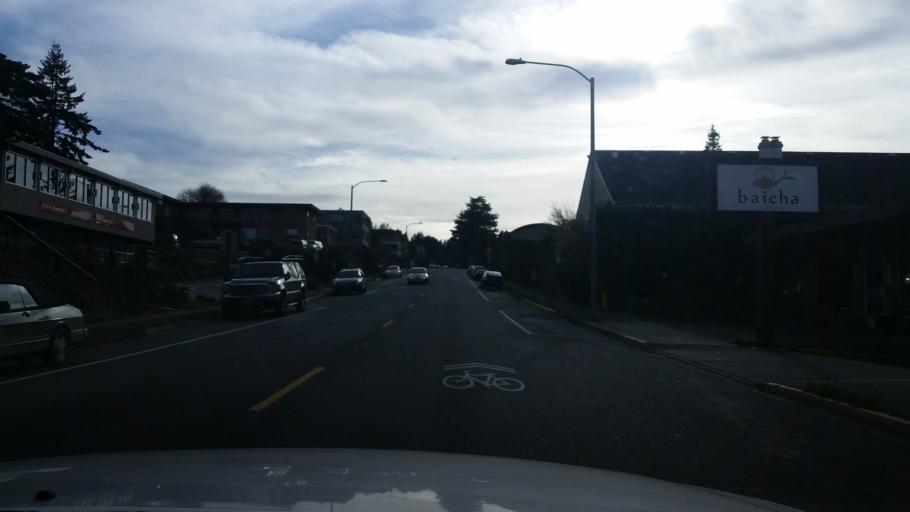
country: US
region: Washington
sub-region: Snohomish County
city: Edmonds
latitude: 47.8054
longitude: -122.3776
